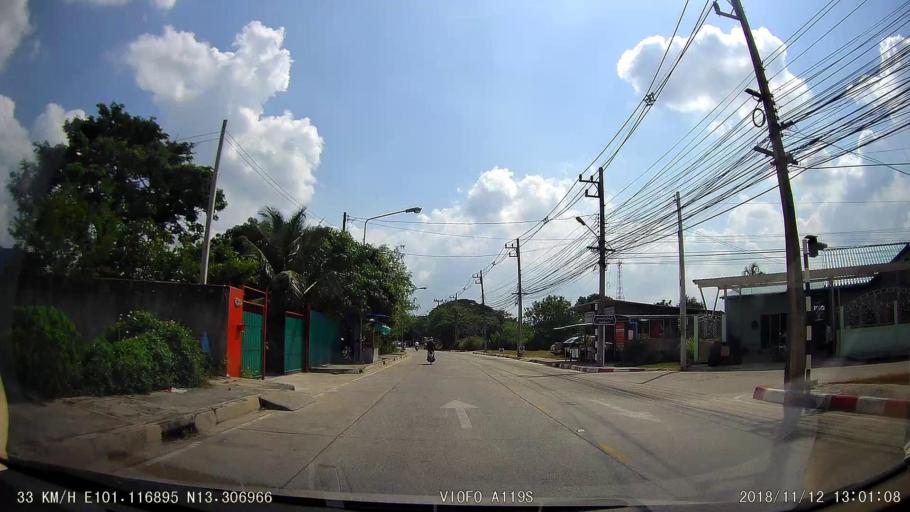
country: TH
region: Chon Buri
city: Ban Bueng
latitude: 13.3068
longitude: 101.1169
